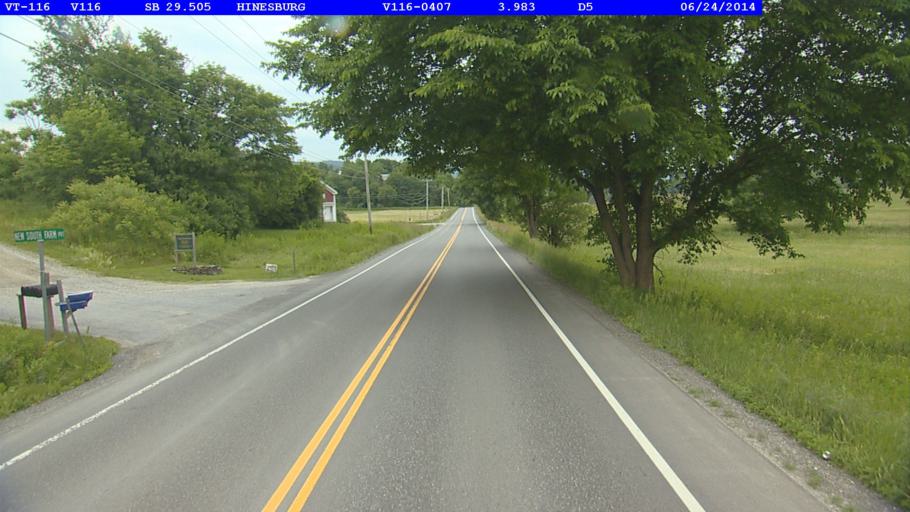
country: US
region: Vermont
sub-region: Chittenden County
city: Hinesburg
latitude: 44.3259
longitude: -73.1023
